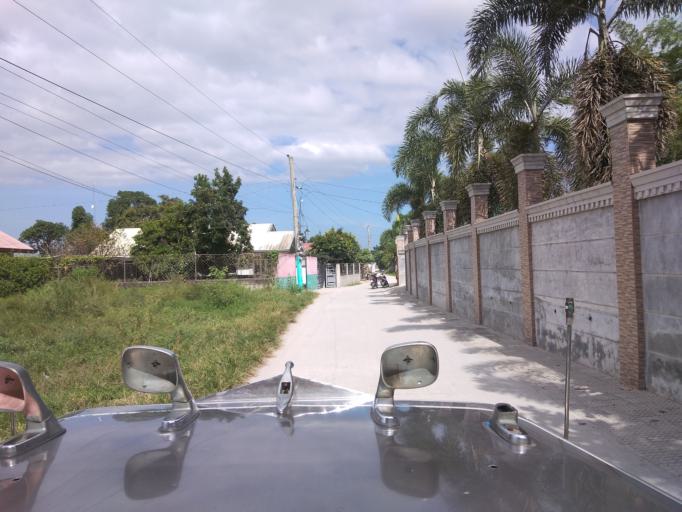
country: PH
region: Central Luzon
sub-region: Province of Pampanga
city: San Patricio
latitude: 15.1087
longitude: 120.7198
